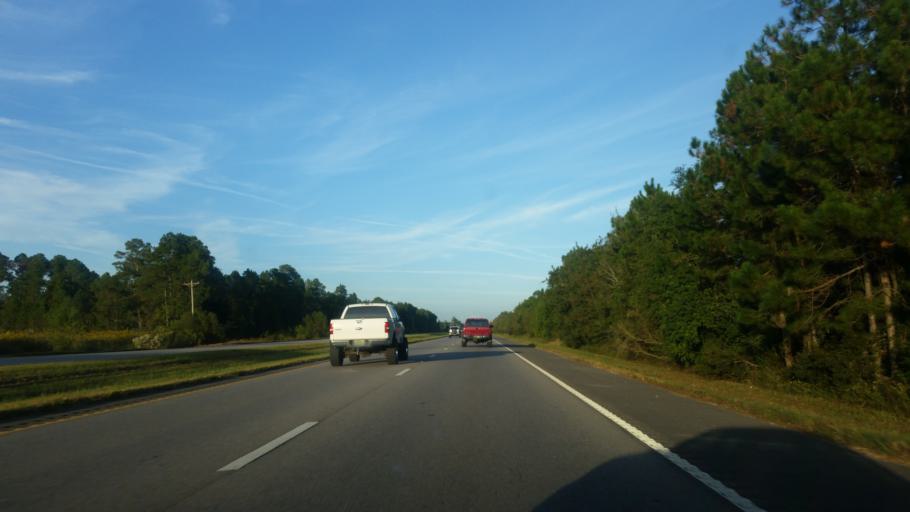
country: US
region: Mississippi
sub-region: Jackson County
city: Moss Point
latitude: 30.4113
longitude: -88.4744
